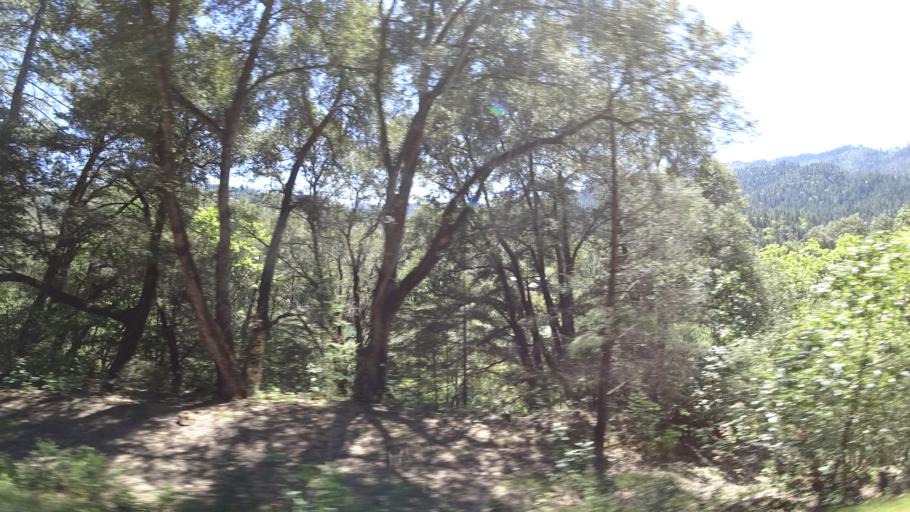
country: US
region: California
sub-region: Trinity County
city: Hayfork
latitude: 40.7418
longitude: -123.2616
